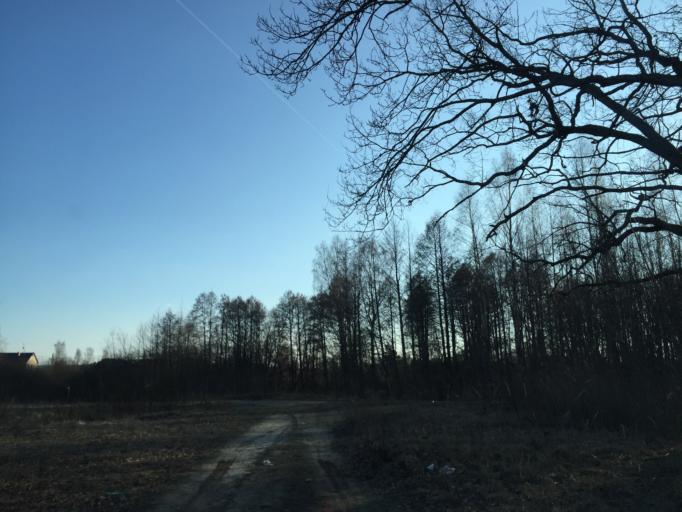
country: LV
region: Riga
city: Bergi
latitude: 56.9791
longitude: 24.2620
